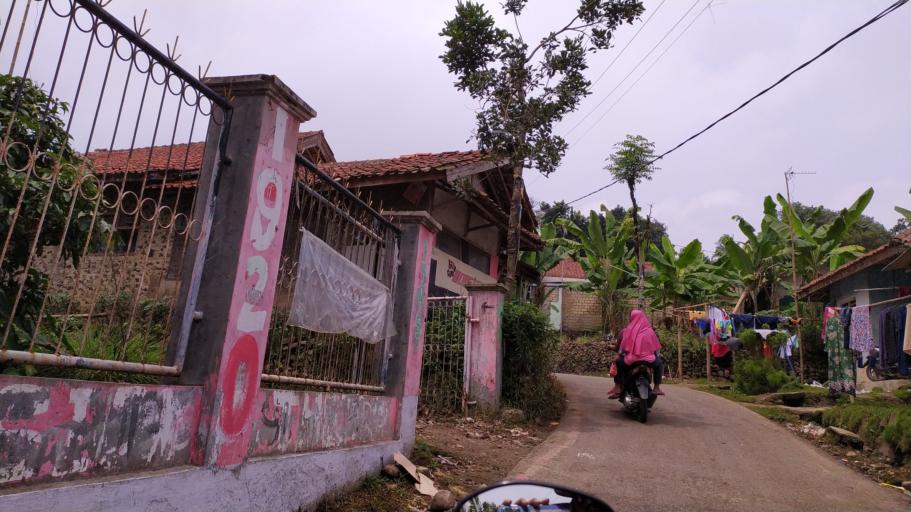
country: ID
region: West Java
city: Ciampea
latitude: -6.6285
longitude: 106.7120
